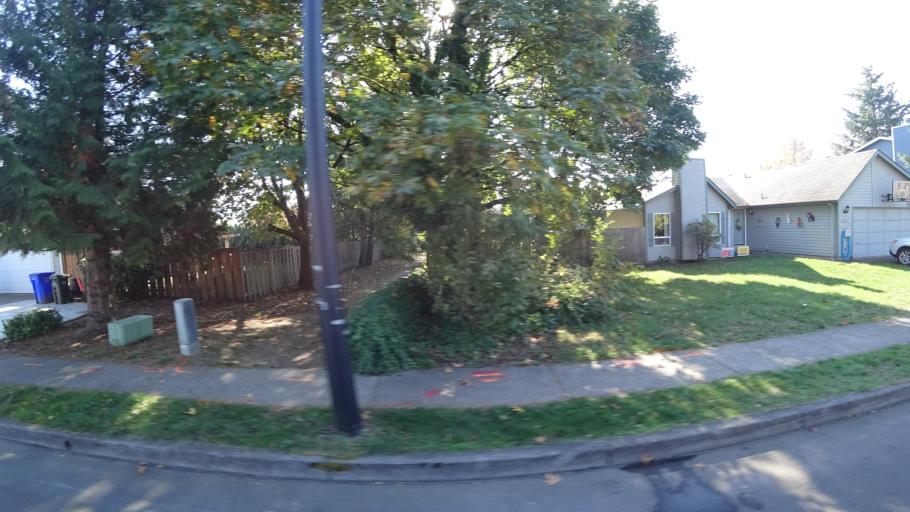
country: US
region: Oregon
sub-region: Multnomah County
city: Gresham
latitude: 45.4941
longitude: -122.4550
